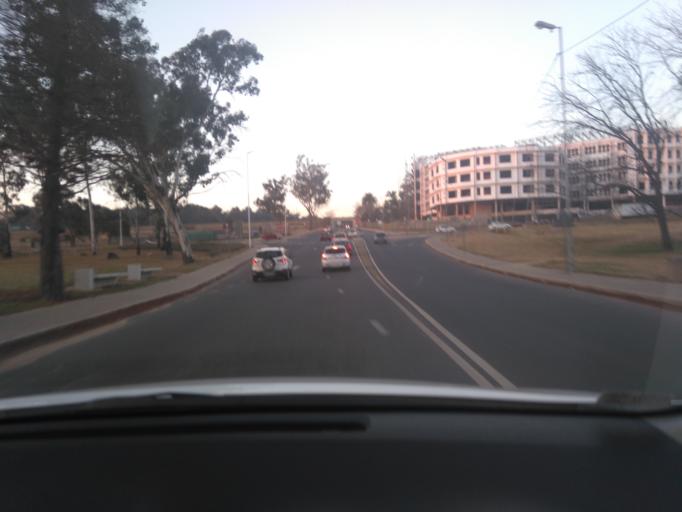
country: ZA
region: Gauteng
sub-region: City of Johannesburg Metropolitan Municipality
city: Modderfontein
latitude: -26.1004
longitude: 28.1584
